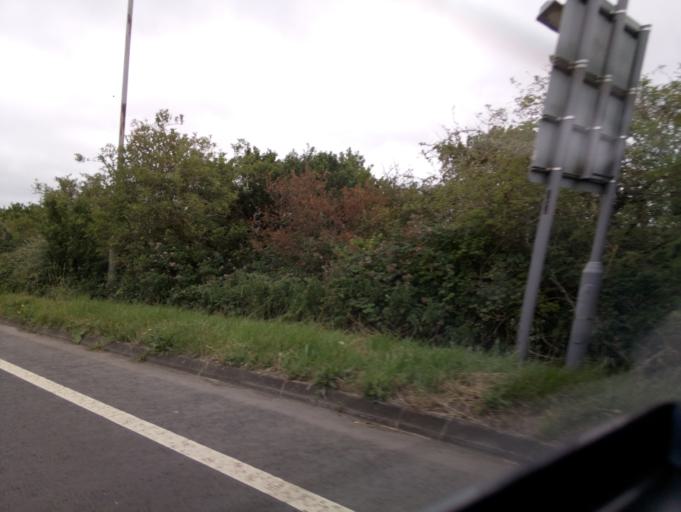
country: GB
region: England
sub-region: Gloucestershire
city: Tewkesbury
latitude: 51.9557
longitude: -2.1581
